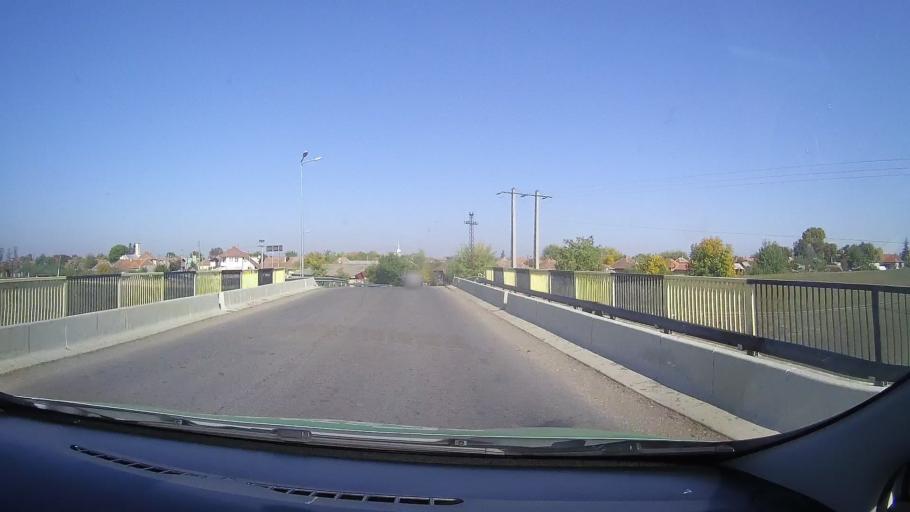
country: RO
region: Satu Mare
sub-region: Comuna Berveni
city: Berveni
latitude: 47.7484
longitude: 22.4731
